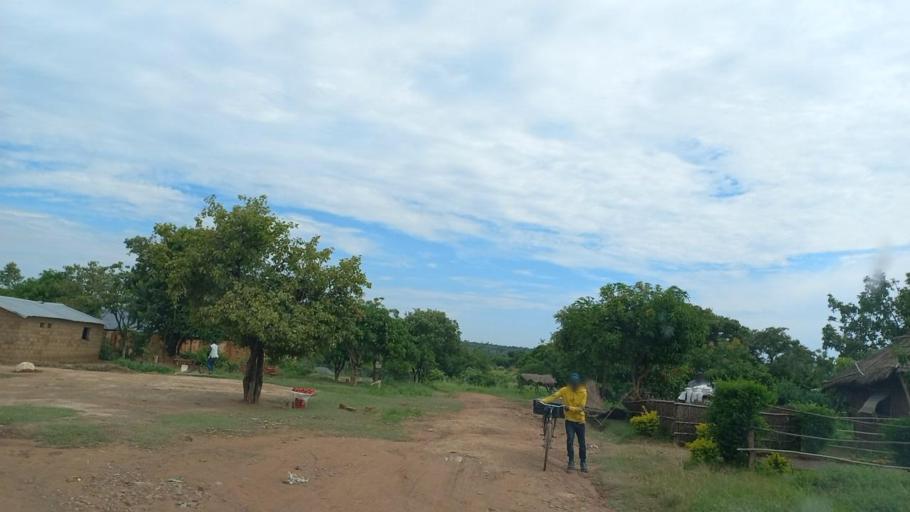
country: ZM
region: Copperbelt
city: Kitwe
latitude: -12.8675
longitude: 28.3349
